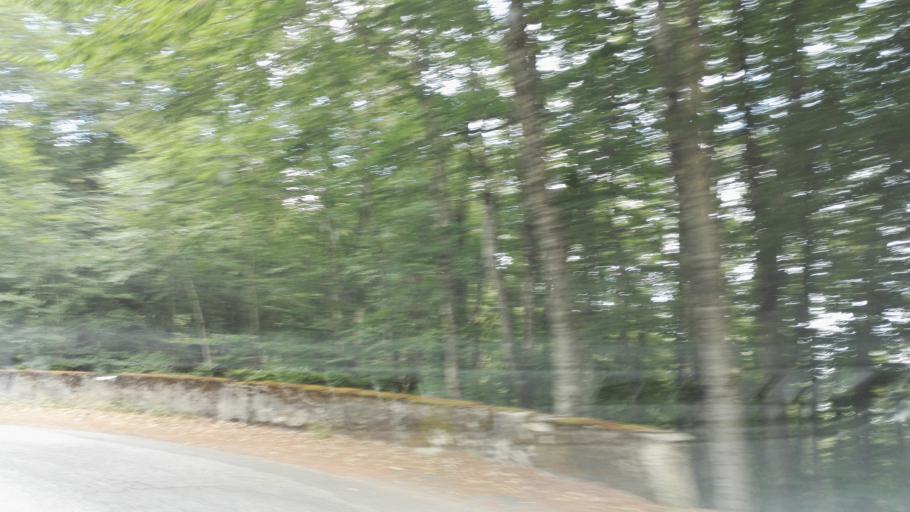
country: IT
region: Calabria
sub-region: Provincia di Vibo-Valentia
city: Nardodipace
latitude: 38.4938
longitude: 16.3434
